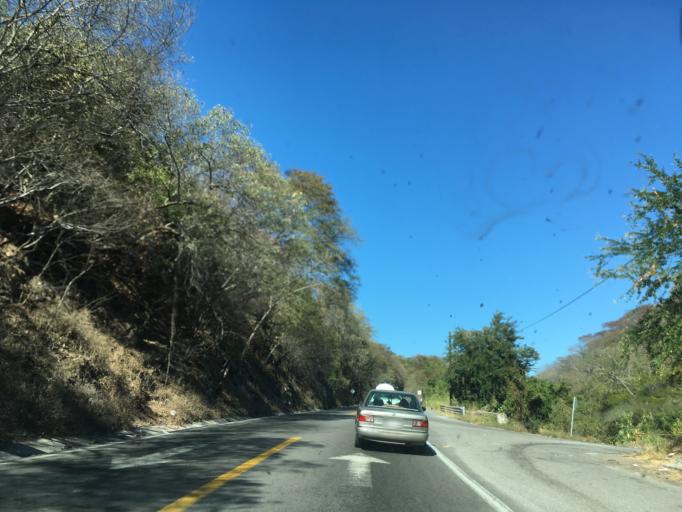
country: MX
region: Michoacan
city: Nueva Italia de Ruiz
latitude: 19.0803
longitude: -102.0638
